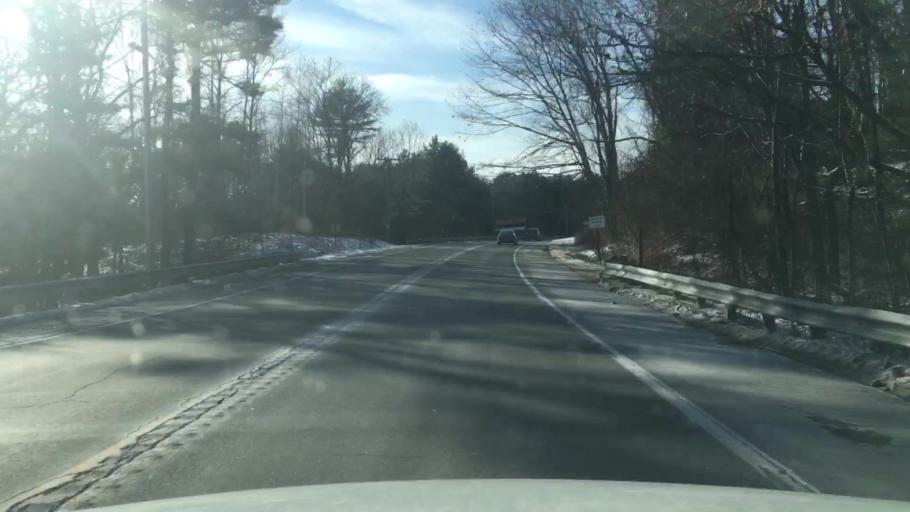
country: US
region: Maine
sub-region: Lincoln County
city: Wiscasset
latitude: 43.9649
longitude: -69.7210
